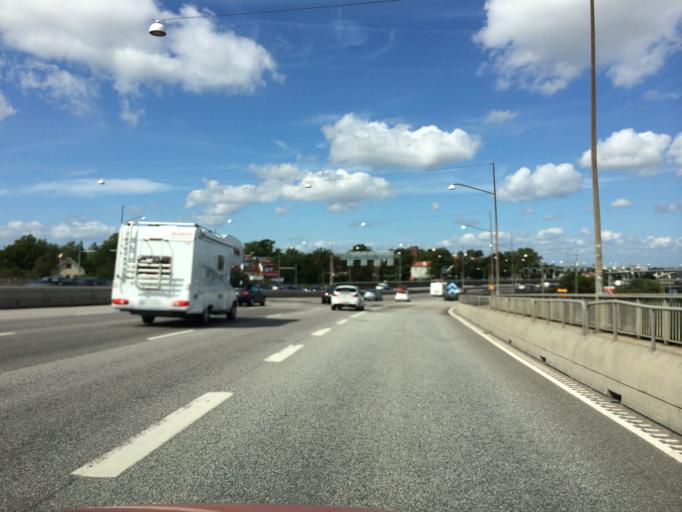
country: SE
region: Stockholm
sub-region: Solna Kommun
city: Solna
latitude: 59.3192
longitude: 17.9980
